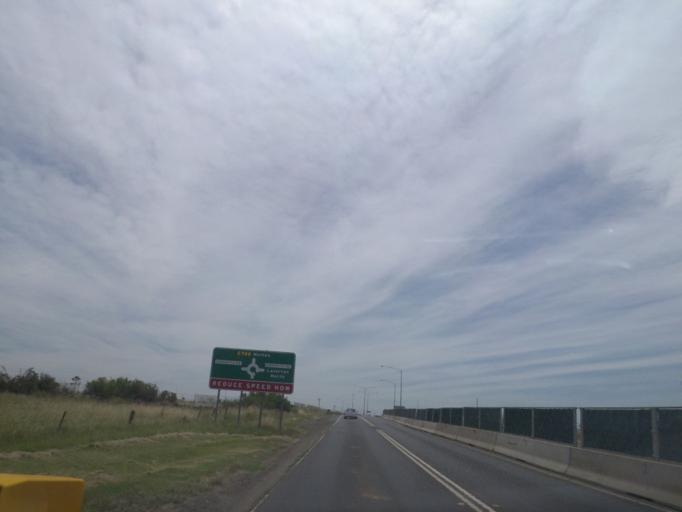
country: AU
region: Victoria
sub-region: Wyndham
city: Tarneit
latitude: -37.8219
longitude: 144.6932
